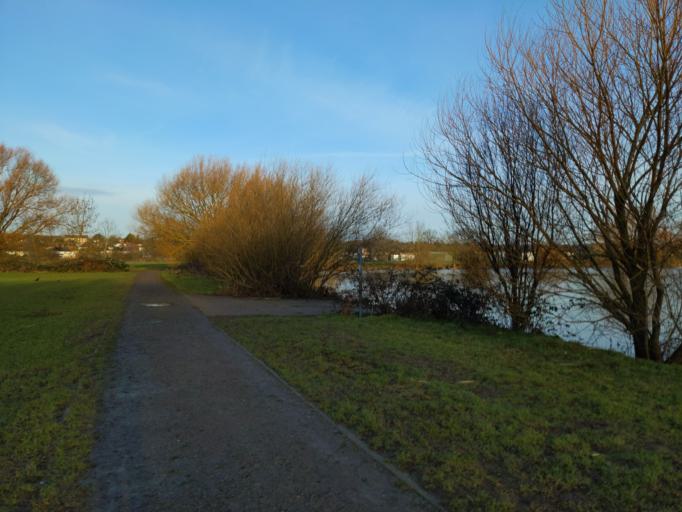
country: GB
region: England
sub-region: Essex
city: Chigwell
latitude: 51.6292
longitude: 0.0593
